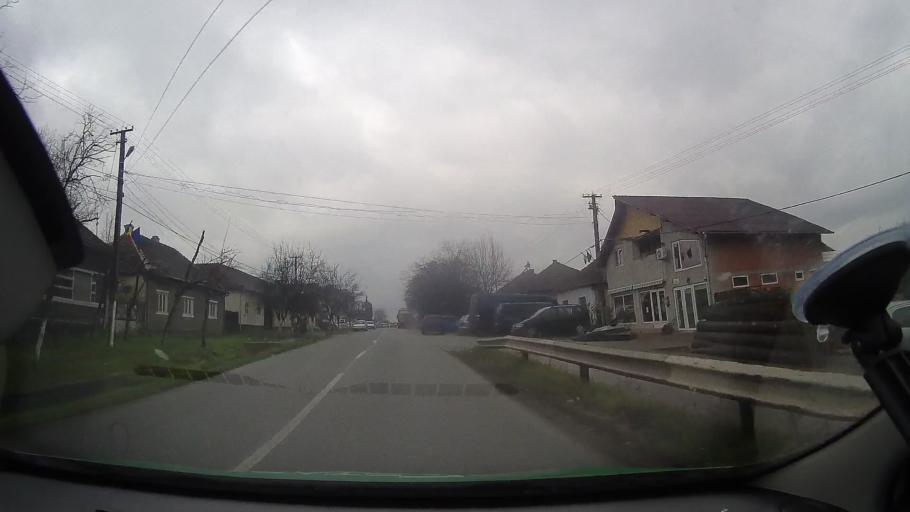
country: RO
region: Arad
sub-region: Comuna Gurahont
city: Gurahont
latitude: 46.2703
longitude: 22.3439
